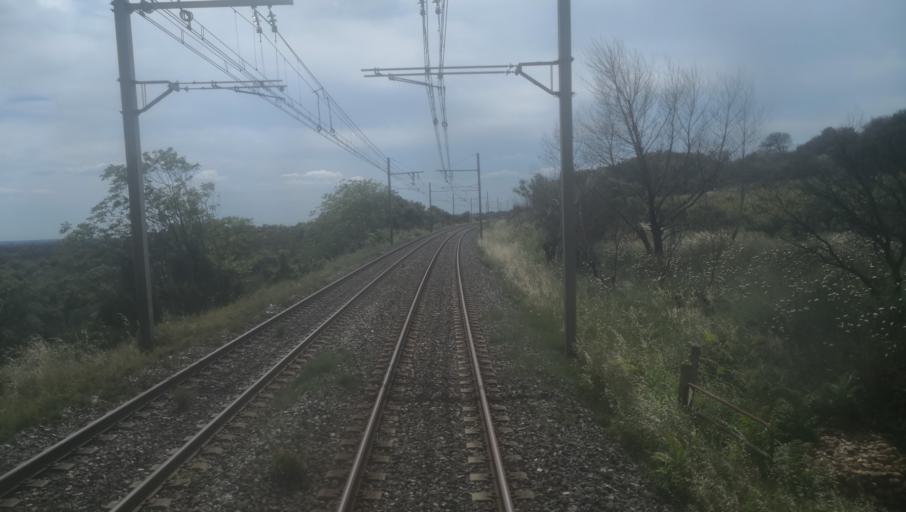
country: FR
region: Languedoc-Roussillon
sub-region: Departement du Gard
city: Jonquieres-Saint-Vincent
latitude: 43.8001
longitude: 4.5855
